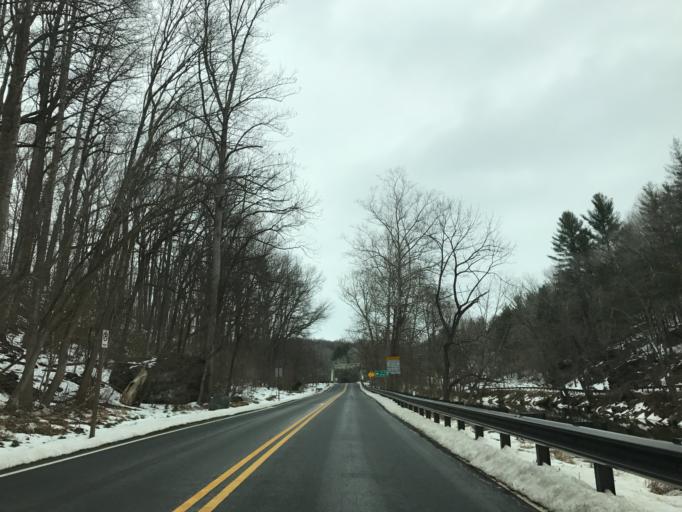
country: US
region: Maryland
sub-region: Harford County
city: Jarrettsville
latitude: 39.6399
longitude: -76.4125
